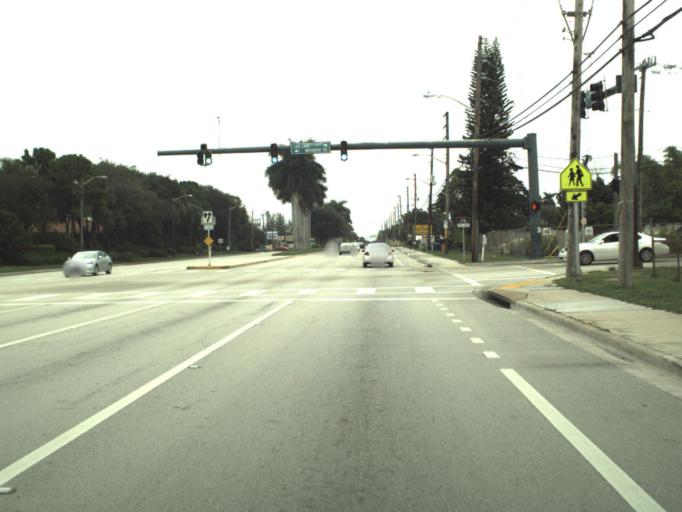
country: US
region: Florida
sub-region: Palm Beach County
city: North Palm Beach
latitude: 26.7922
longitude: -80.1068
